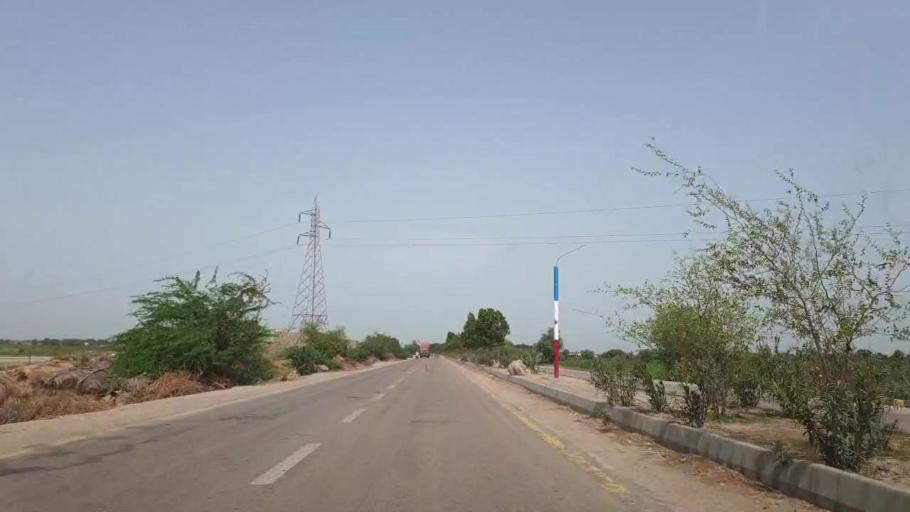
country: PK
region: Sindh
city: Sakrand
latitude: 26.1609
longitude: 68.2688
